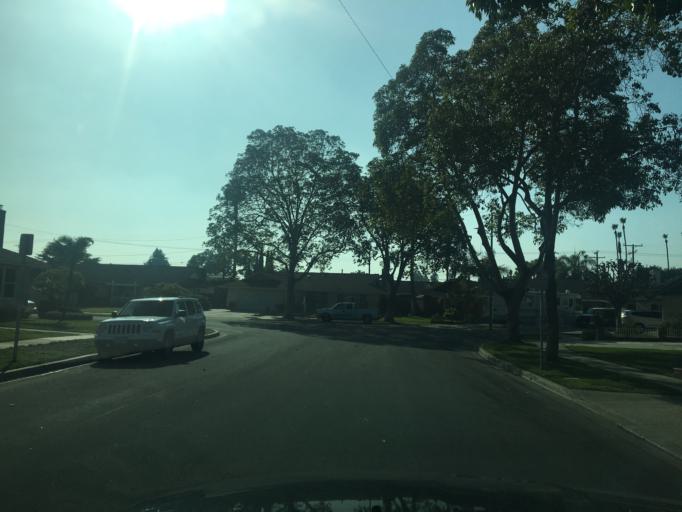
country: US
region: California
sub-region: Orange County
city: Tustin
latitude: 33.7339
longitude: -117.8206
